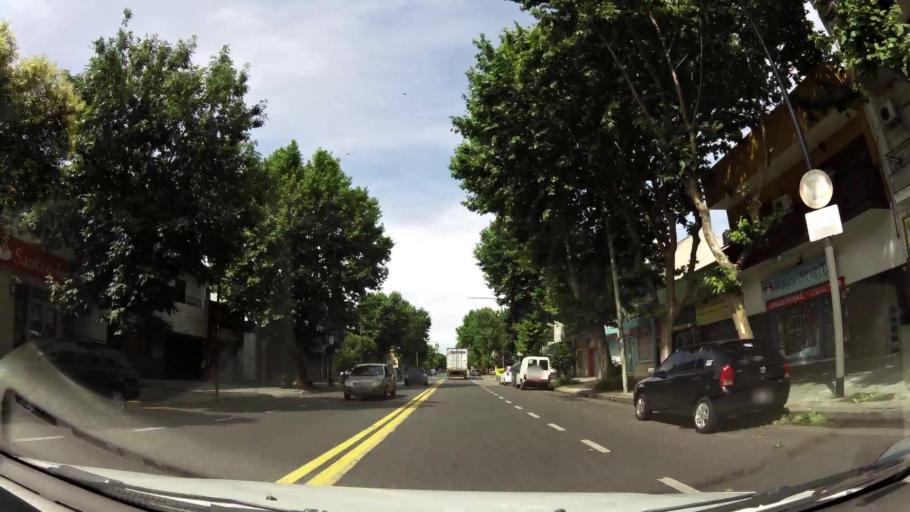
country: AR
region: Buenos Aires
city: San Justo
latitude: -34.6530
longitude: -58.5178
